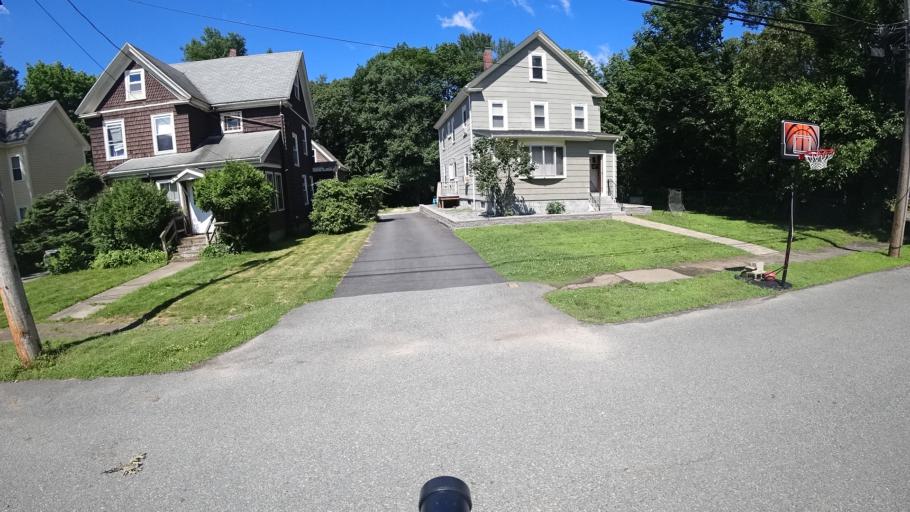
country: US
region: Massachusetts
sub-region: Norfolk County
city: Dedham
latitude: 42.2572
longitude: -71.1515
